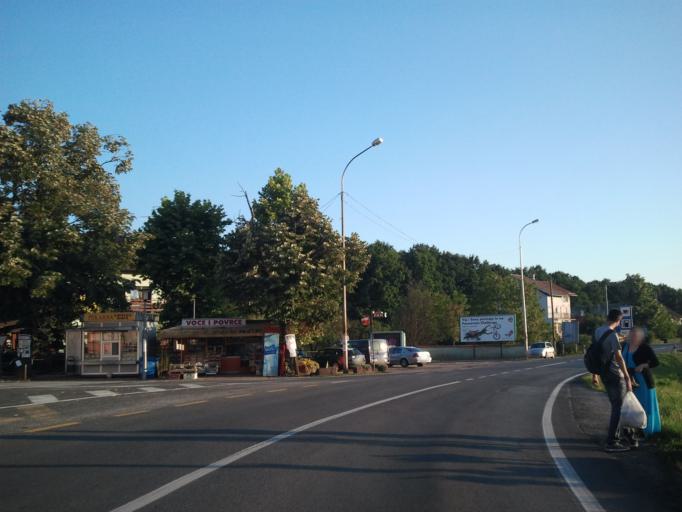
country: HR
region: Sisacko-Moslavacka
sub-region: Grad Sisak
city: Sisak
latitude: 45.4436
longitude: 16.3678
